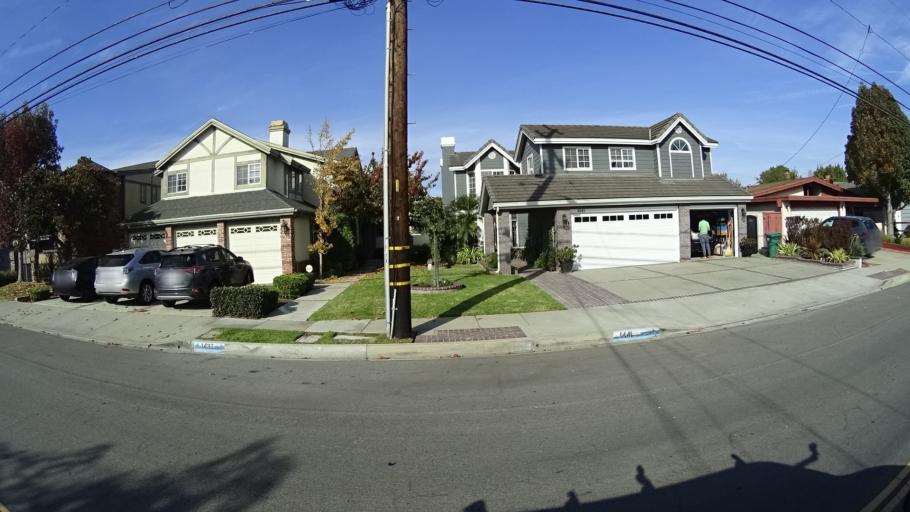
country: US
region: California
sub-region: Los Angeles County
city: Hermosa Beach
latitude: 33.8801
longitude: -118.3884
